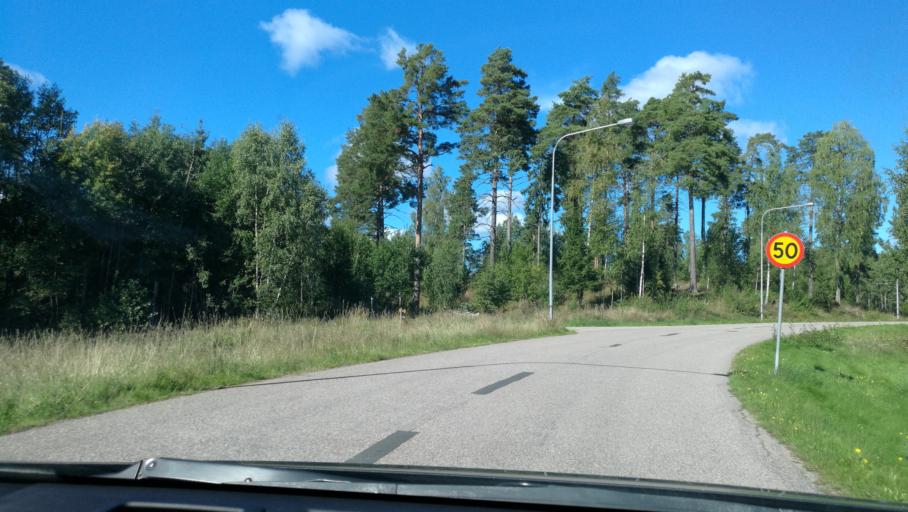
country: SE
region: Vaestmanland
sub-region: Surahammars Kommun
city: Surahammar
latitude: 59.6909
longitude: 16.2365
